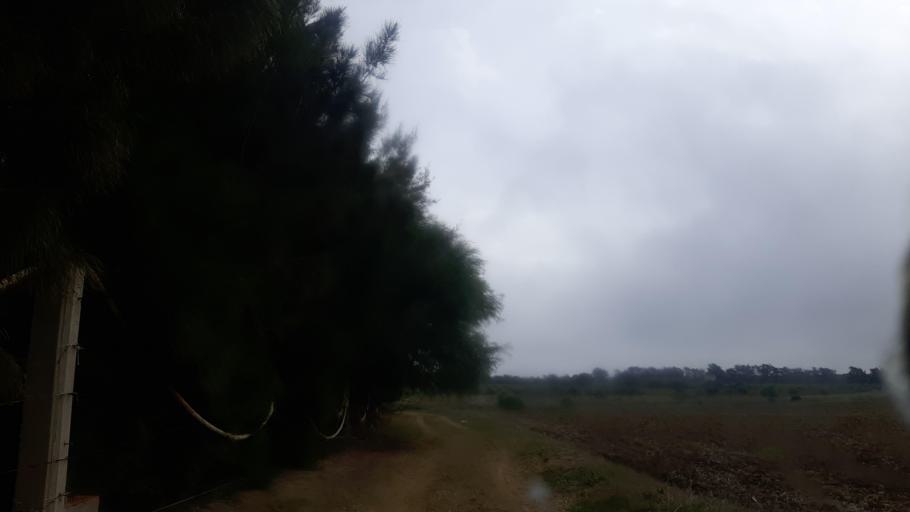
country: TN
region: Nabul
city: Qulaybiyah
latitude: 36.8258
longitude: 11.0364
